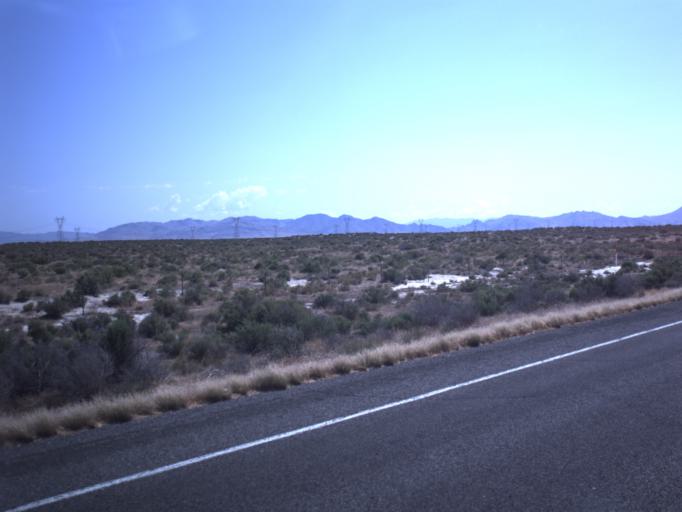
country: US
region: Utah
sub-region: Millard County
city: Delta
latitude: 39.4854
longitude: -112.5335
